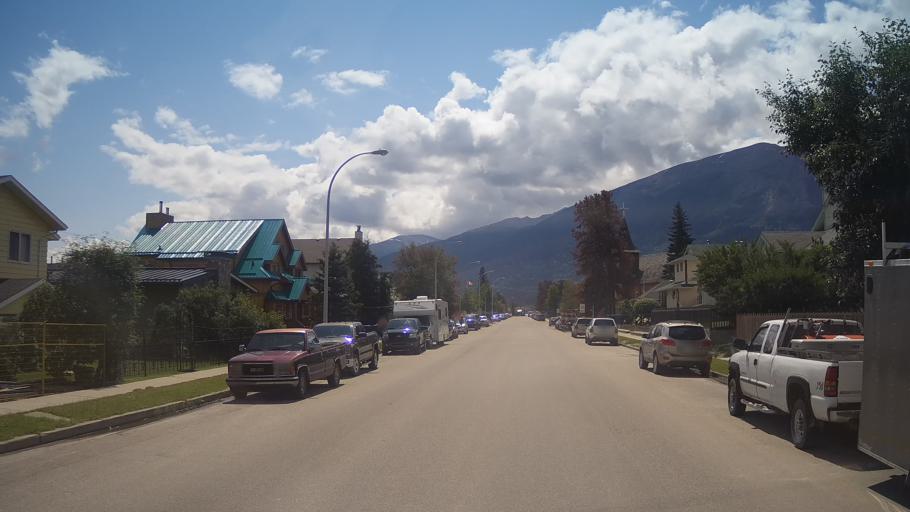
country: CA
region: Alberta
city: Jasper Park Lodge
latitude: 52.8808
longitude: -118.0815
